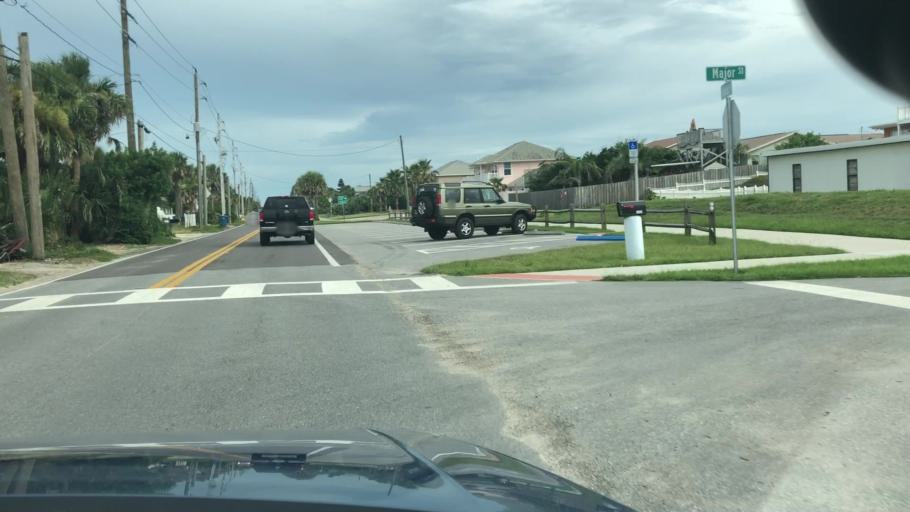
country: US
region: Florida
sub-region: Volusia County
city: Ponce Inlet
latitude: 29.1231
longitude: -80.9530
